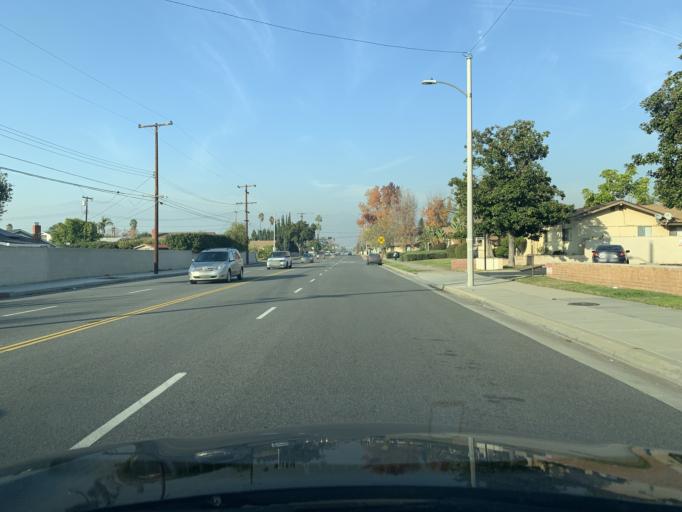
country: US
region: California
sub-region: Los Angeles County
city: Covina
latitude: 34.0906
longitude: -117.8989
